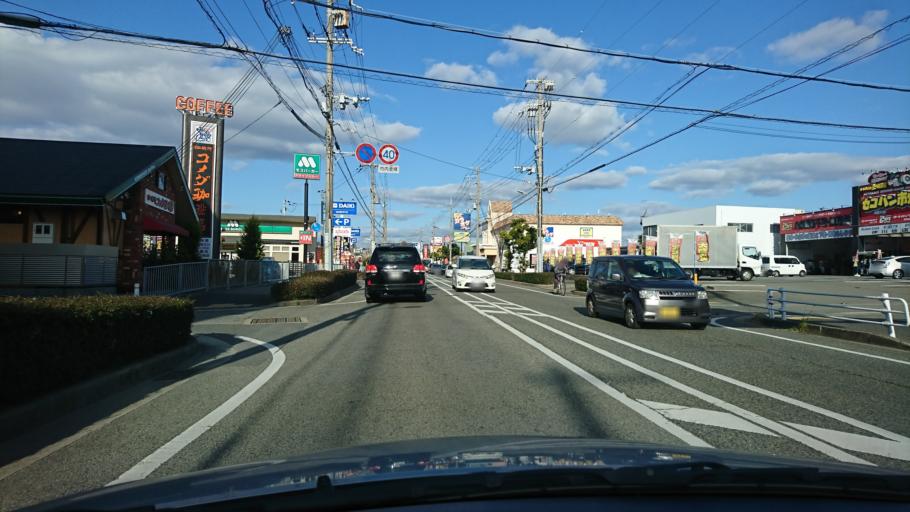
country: JP
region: Hyogo
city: Akashi
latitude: 34.6661
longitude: 135.0031
